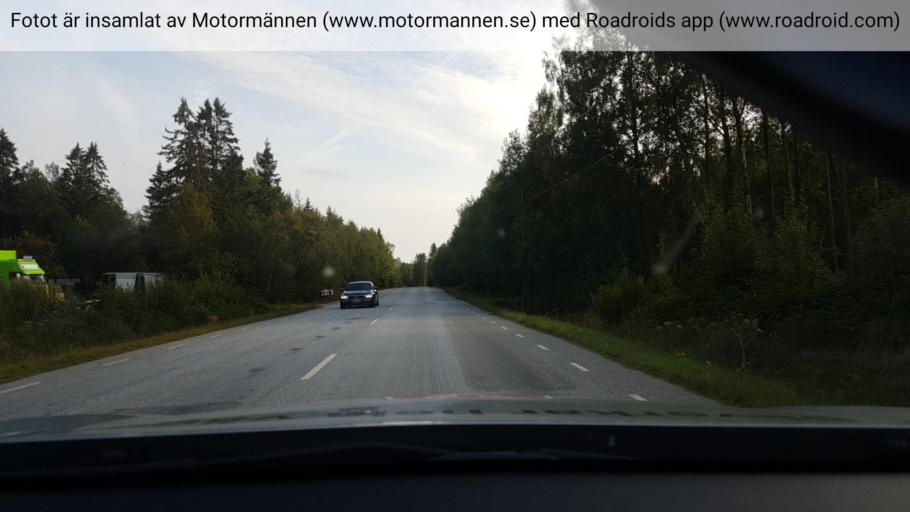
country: SE
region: Vaestra Goetaland
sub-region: Uddevalla Kommun
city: Ljungskile
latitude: 58.1425
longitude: 11.9764
